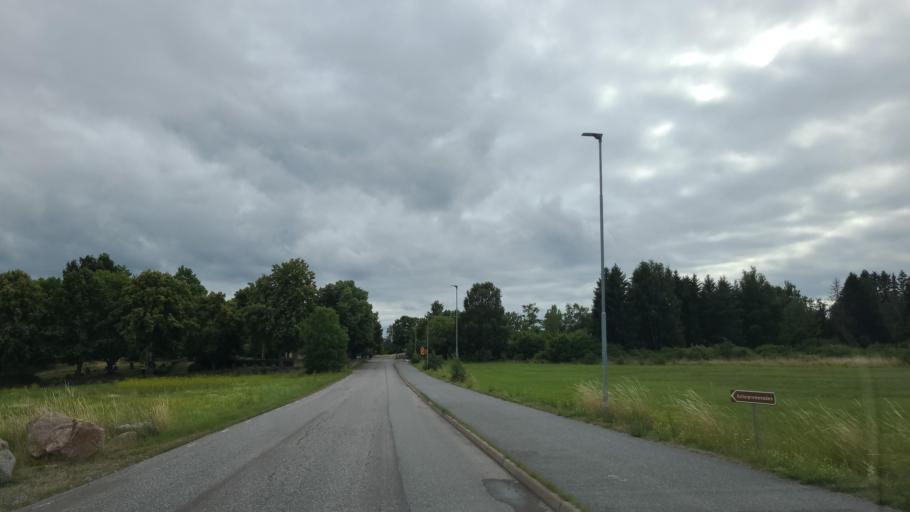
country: SE
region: Stockholm
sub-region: Upplands-Bro Kommun
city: Bro
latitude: 59.5079
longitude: 17.6271
